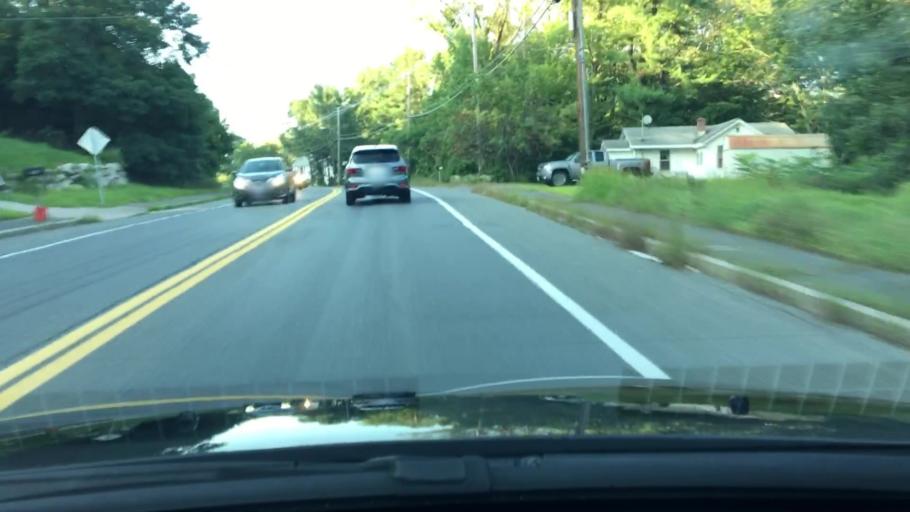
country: US
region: Massachusetts
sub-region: Worcester County
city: Shrewsbury
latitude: 42.3142
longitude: -71.7174
